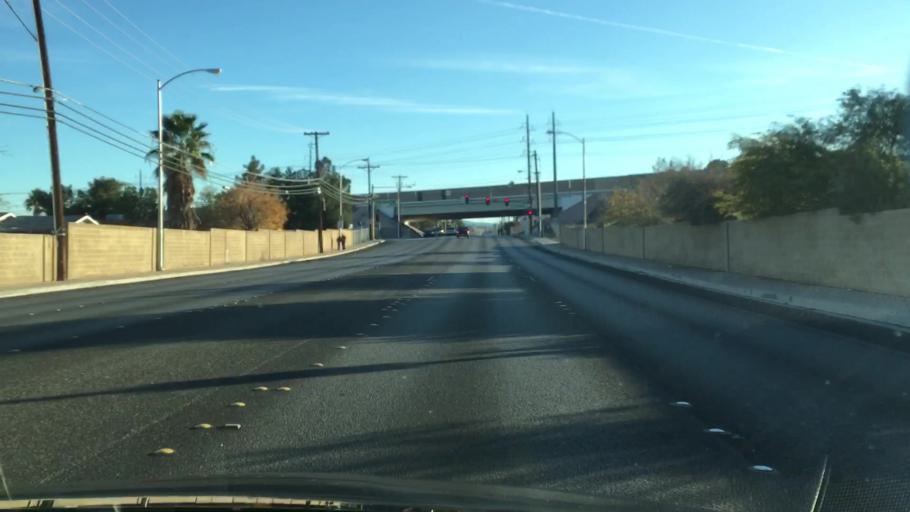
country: US
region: Nevada
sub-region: Clark County
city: Whitney
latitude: 36.0942
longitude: -115.0732
